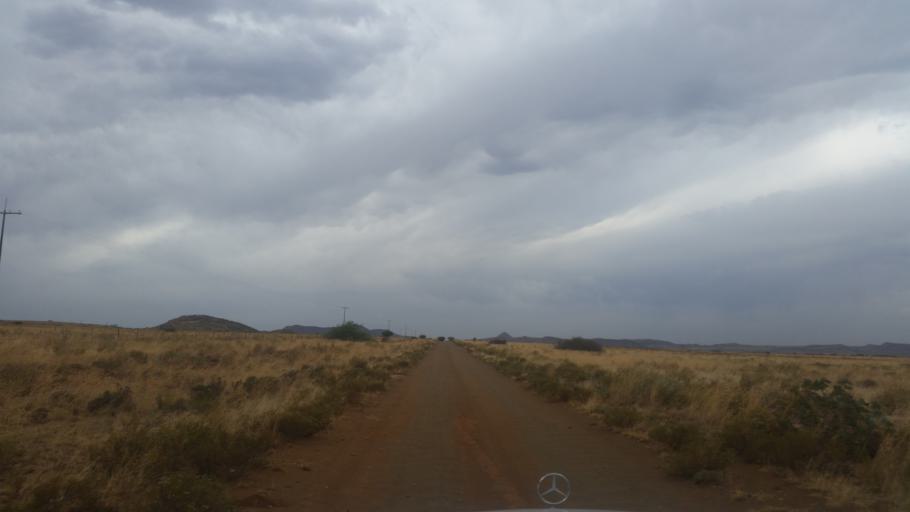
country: ZA
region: Orange Free State
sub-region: Xhariep District Municipality
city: Trompsburg
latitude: -30.5054
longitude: 25.9436
